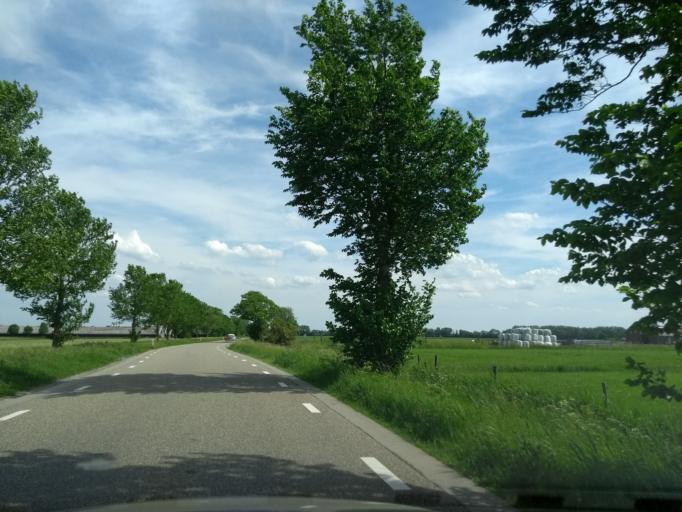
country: NL
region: Groningen
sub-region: Gemeente Zuidhorn
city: Aduard
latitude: 53.2709
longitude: 6.4321
